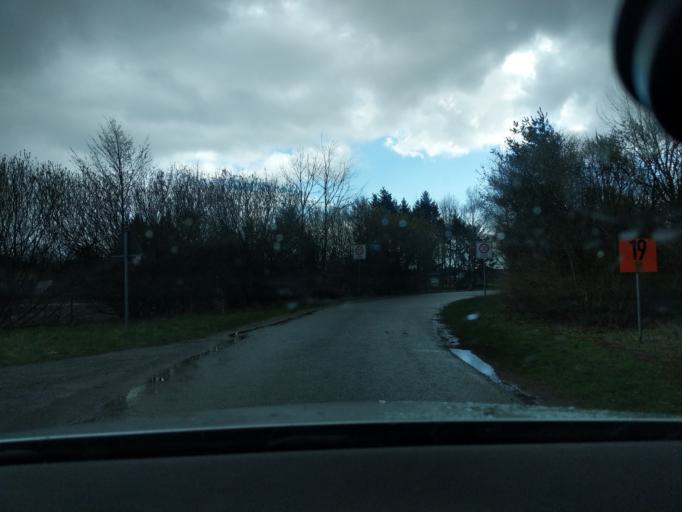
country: DE
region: Lower Saxony
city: Kranenburg
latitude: 53.6294
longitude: 9.2056
